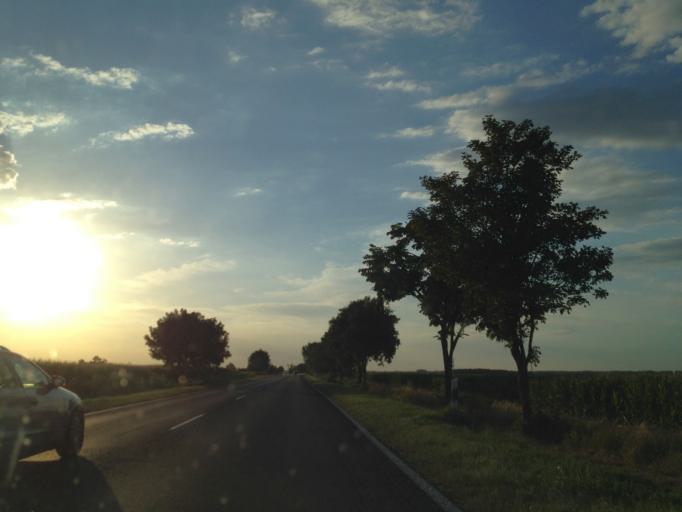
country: HU
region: Gyor-Moson-Sopron
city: Kimle
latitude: 47.7948
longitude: 17.3948
